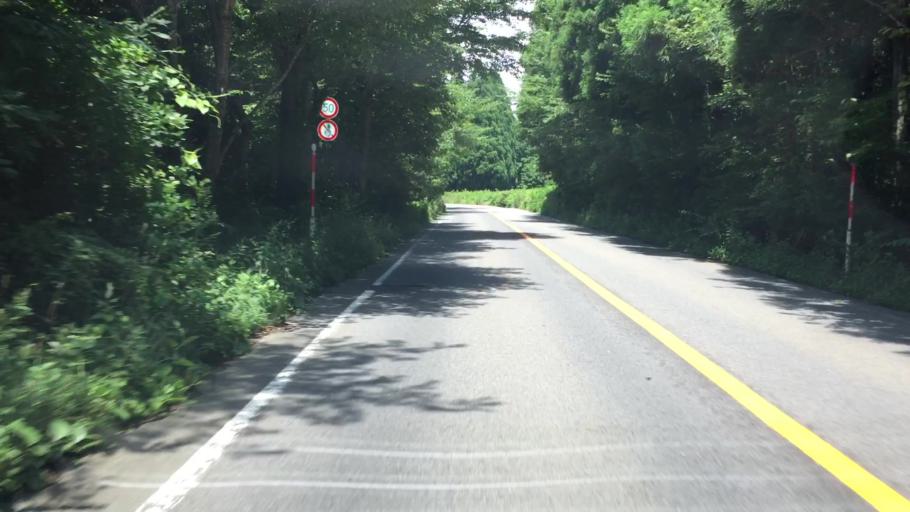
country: JP
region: Tochigi
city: Kuroiso
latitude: 37.0233
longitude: 139.9490
